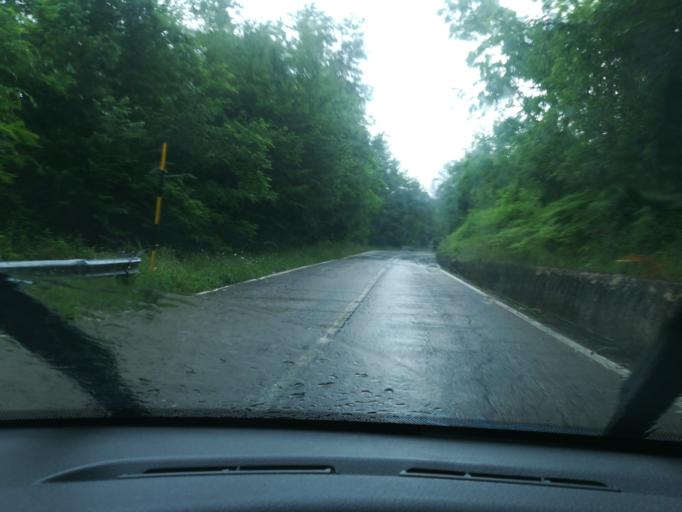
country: IT
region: The Marches
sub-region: Province of Fermo
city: Amandola
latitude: 42.9989
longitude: 13.3344
